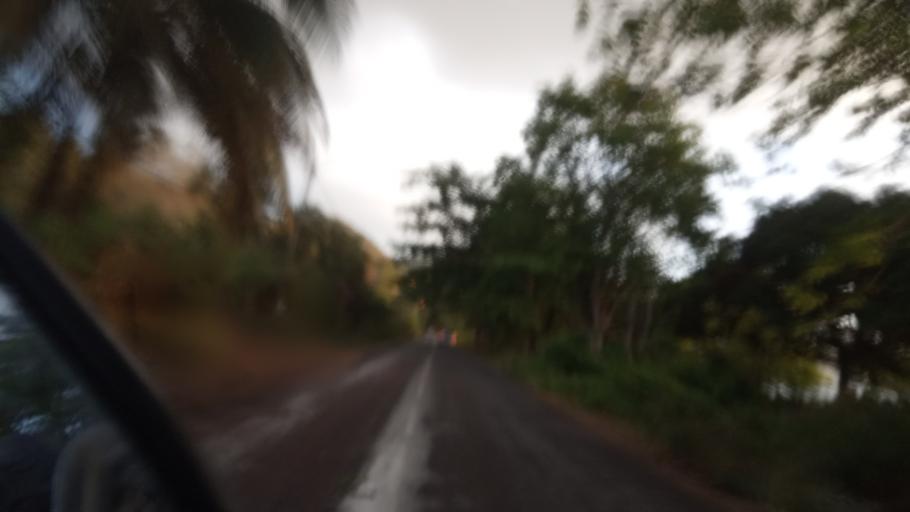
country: YT
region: Kani-Keli
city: Kani Keli
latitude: -12.9302
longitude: 45.1042
